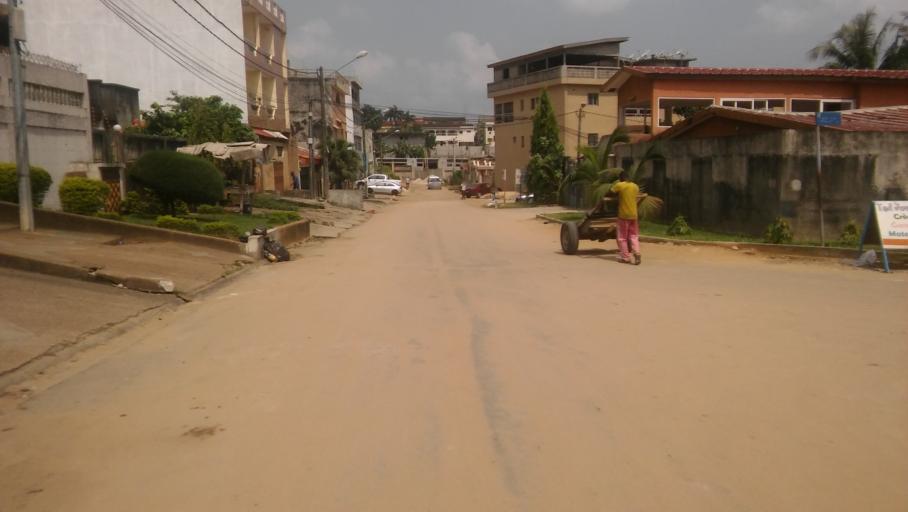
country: CI
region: Lagunes
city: Abidjan
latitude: 5.3588
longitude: -3.9767
